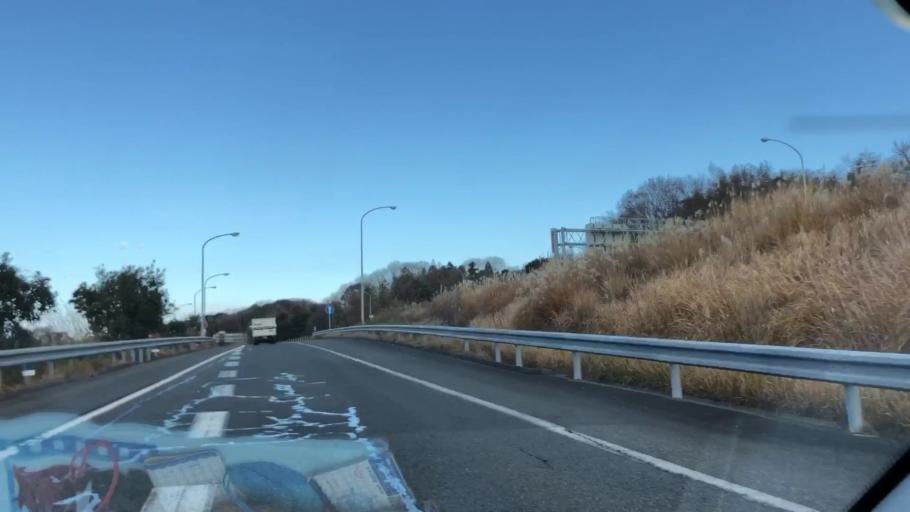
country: JP
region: Chiba
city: Kisarazu
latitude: 35.3794
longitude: 139.9781
